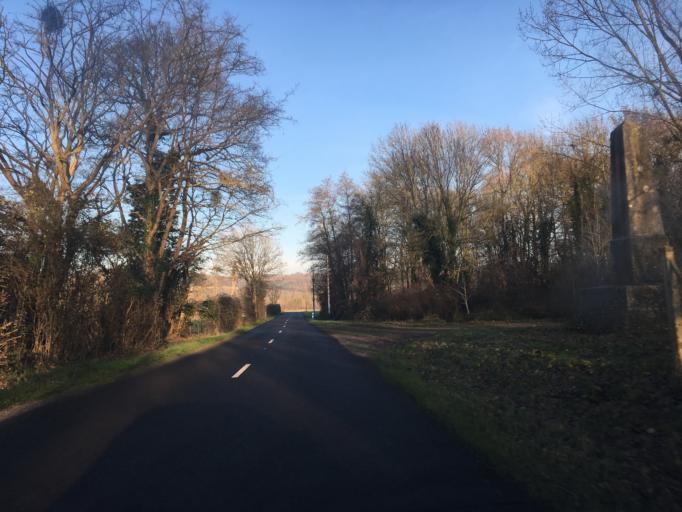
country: FR
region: Haute-Normandie
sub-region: Departement de l'Eure
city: Houlbec-Cocherel
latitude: 49.0528
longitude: 1.3215
